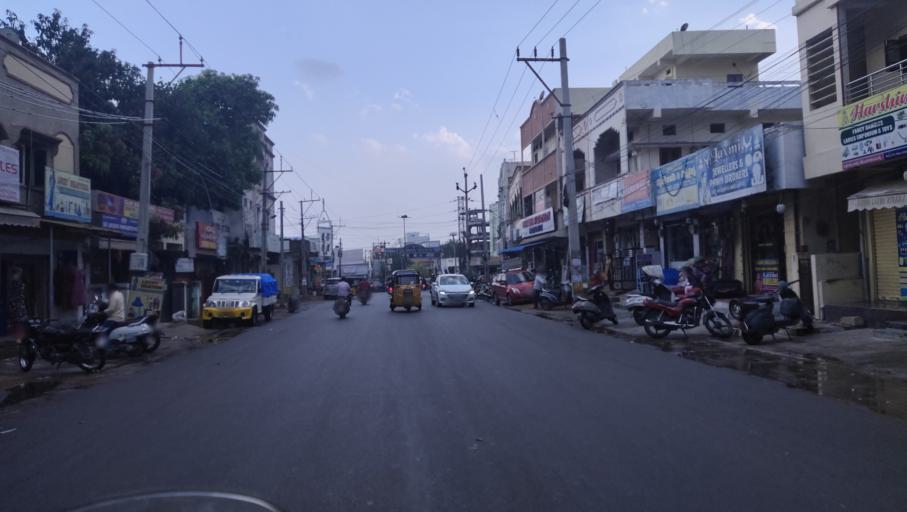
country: IN
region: Telangana
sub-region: Rangareddi
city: Lal Bahadur Nagar
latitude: 17.3222
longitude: 78.5651
